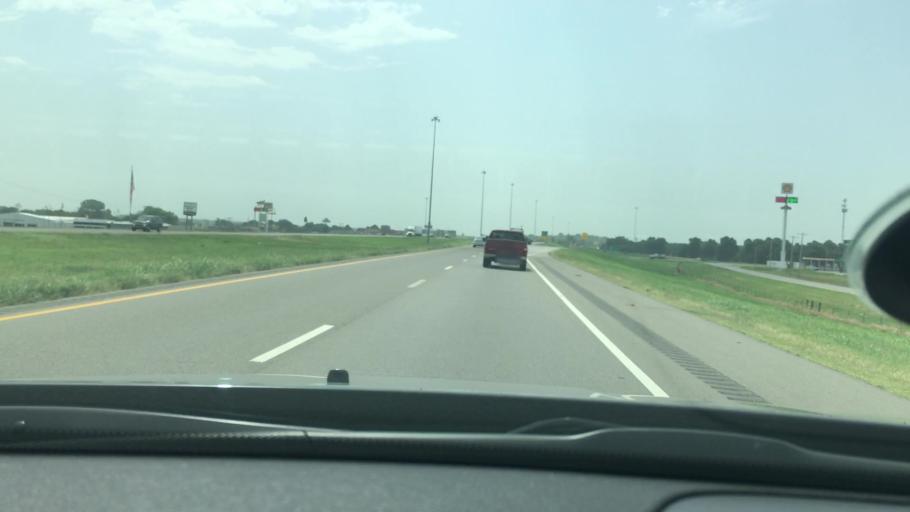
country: US
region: Oklahoma
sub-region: Garvin County
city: Pauls Valley
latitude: 34.7441
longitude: -97.2679
